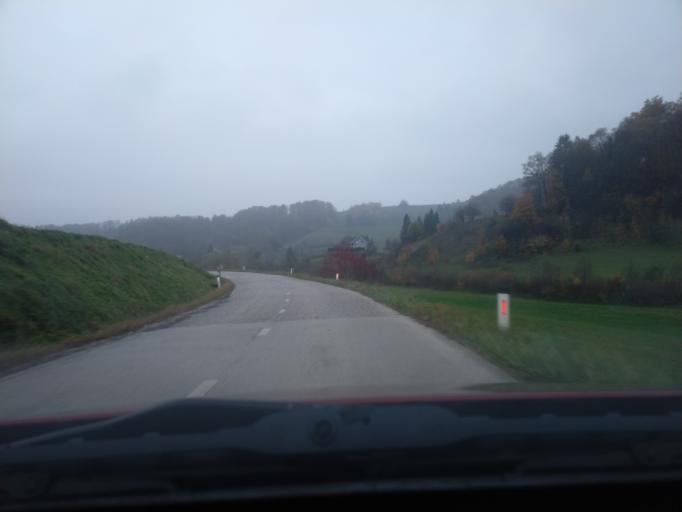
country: SI
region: Kungota
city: Zgornja Kungota
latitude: 46.6642
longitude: 15.6107
